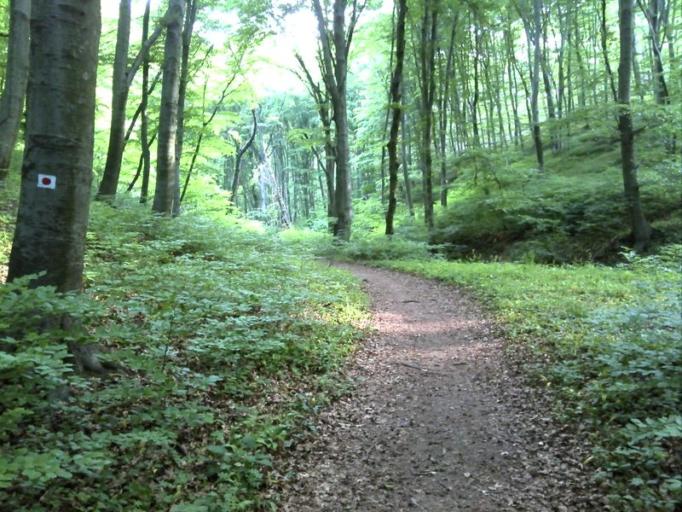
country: HU
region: Baranya
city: Pecs
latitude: 46.0965
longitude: 18.1715
